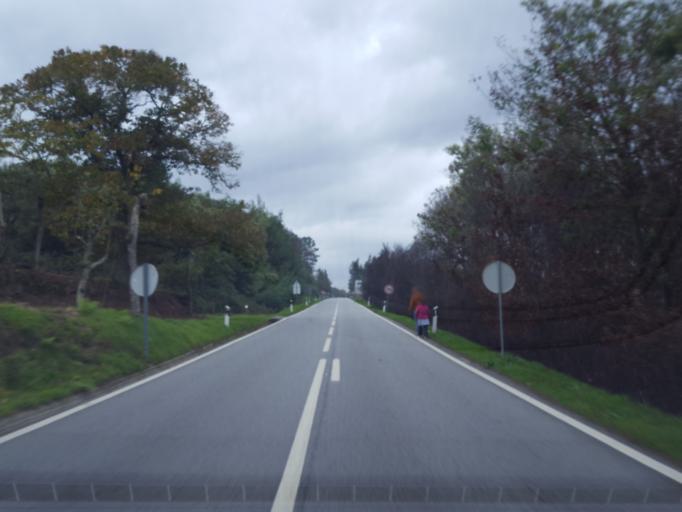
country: PT
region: Porto
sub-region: Marco de Canaveses
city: Marco de Canavezes
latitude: 41.1555
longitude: -8.1433
